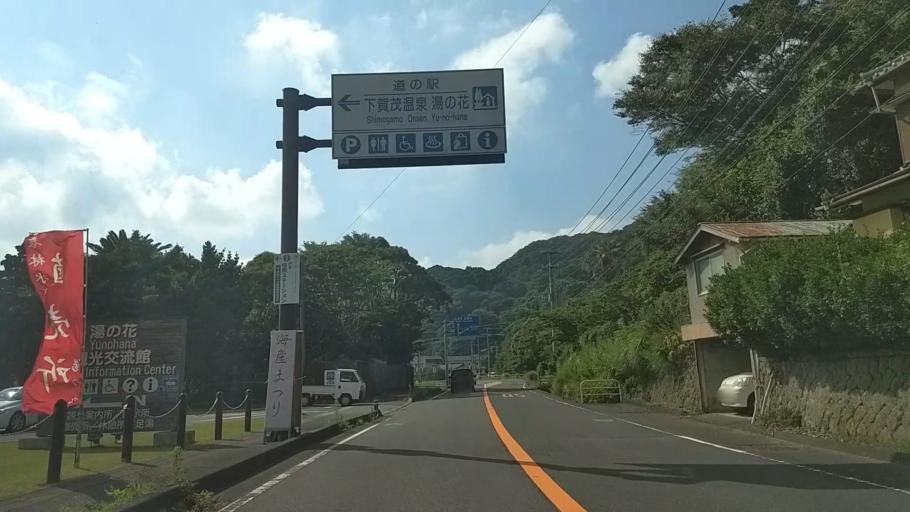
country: JP
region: Shizuoka
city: Shimoda
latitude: 34.6500
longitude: 138.8670
